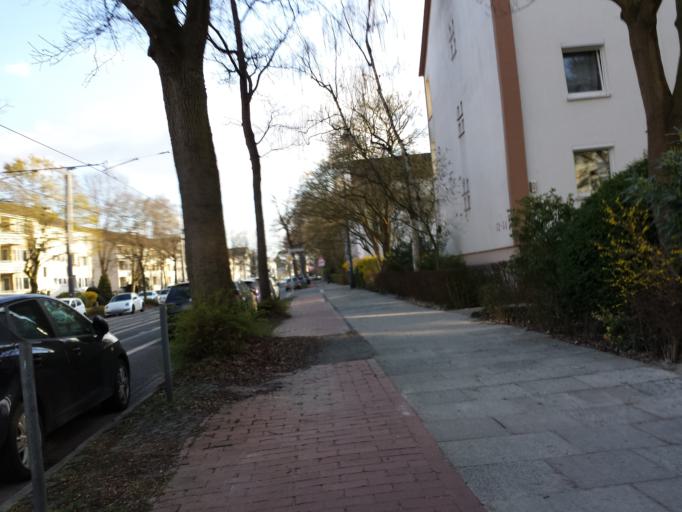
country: DE
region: Bremen
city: Bremen
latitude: 53.0962
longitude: 8.8381
